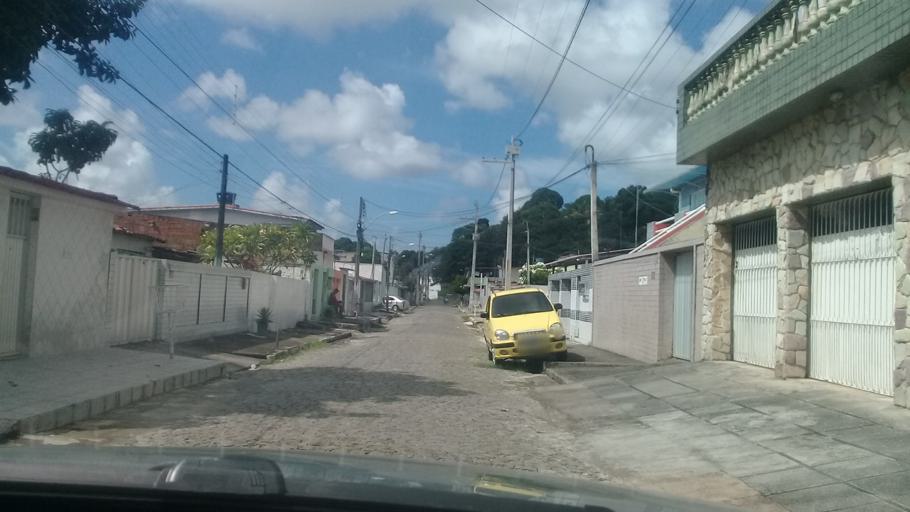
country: BR
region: Pernambuco
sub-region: Jaboatao Dos Guararapes
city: Jaboatao dos Guararapes
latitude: -8.1260
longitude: -34.9507
